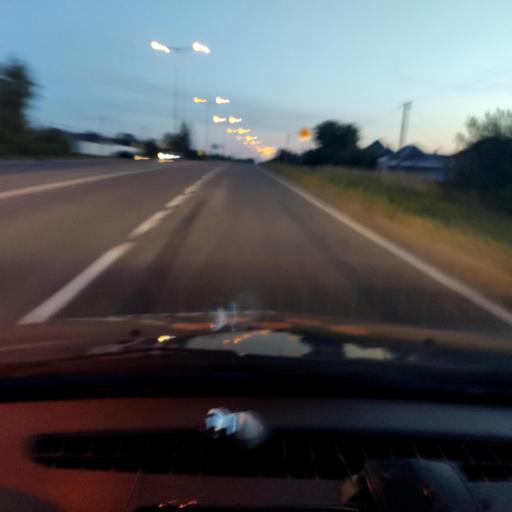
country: RU
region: Belgorod
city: Gubkin
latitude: 51.2736
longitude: 37.5855
